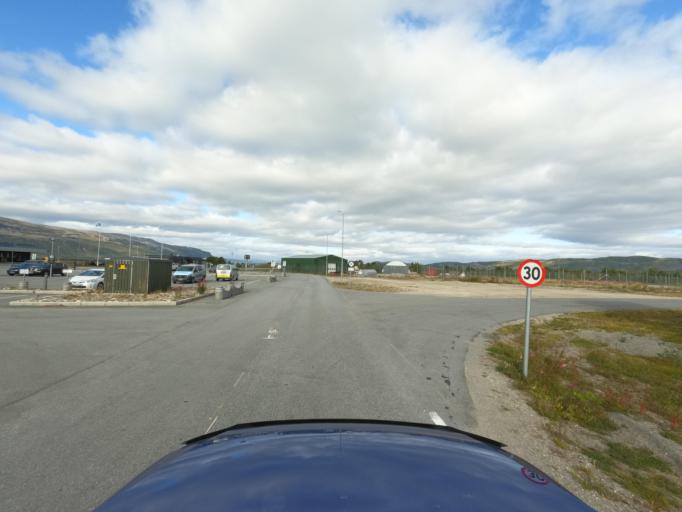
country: NO
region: Finnmark Fylke
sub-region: Porsanger
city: Lakselv
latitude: 70.0659
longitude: 24.9845
